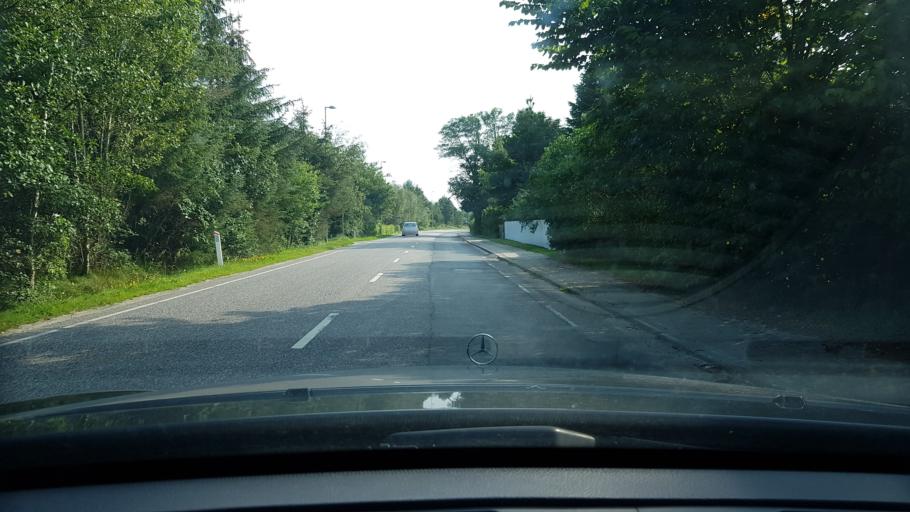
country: DK
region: North Denmark
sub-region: Mariagerfjord Kommune
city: Hadsund
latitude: 56.8125
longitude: 10.2709
